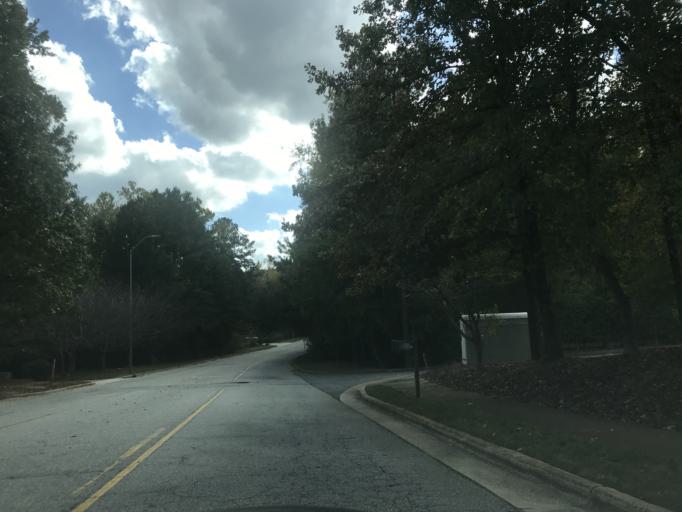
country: US
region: North Carolina
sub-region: Wake County
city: Garner
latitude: 35.7287
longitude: -78.6575
